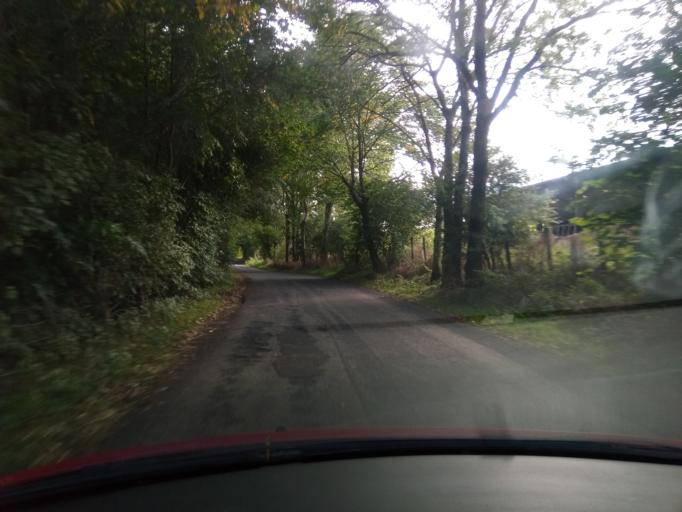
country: GB
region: Scotland
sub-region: The Scottish Borders
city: Kelso
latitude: 55.5016
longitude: -2.3483
